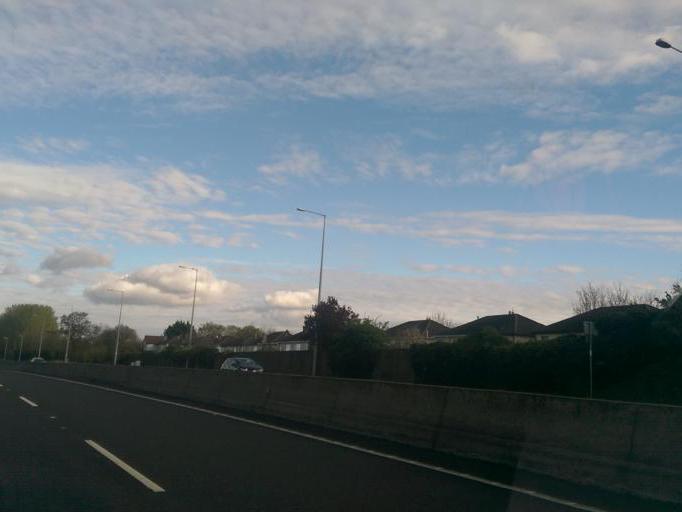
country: IE
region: Leinster
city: Lucan
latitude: 53.3524
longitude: -6.4552
